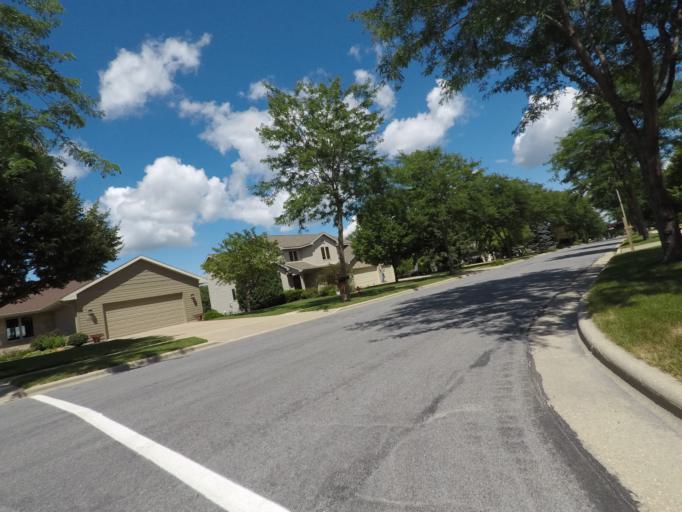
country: US
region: Wisconsin
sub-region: Dane County
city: Middleton
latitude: 43.0708
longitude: -89.5299
